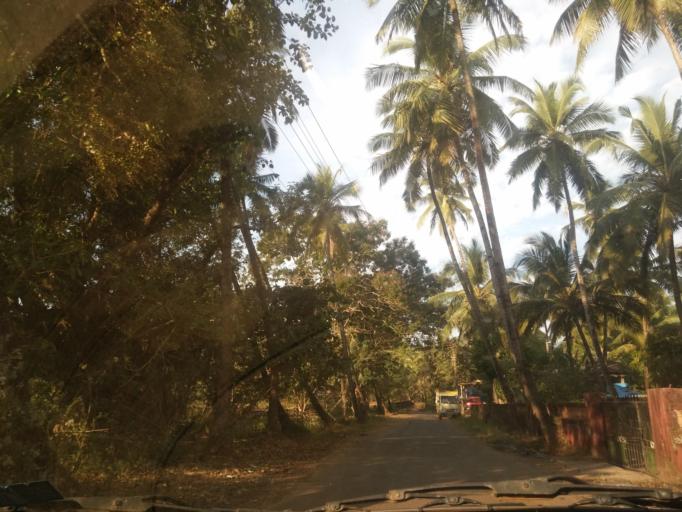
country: IN
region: Goa
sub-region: South Goa
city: Varca
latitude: 15.2402
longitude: 73.9645
